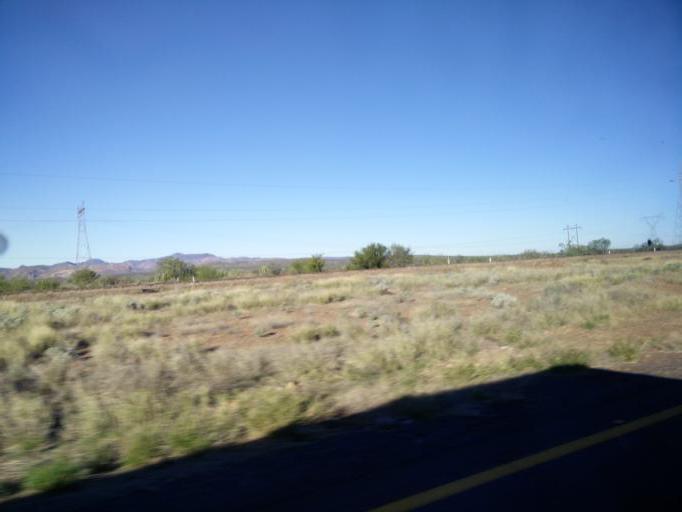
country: MX
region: Sonora
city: Heroica Guaymas
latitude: 28.2032
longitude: -111.0074
